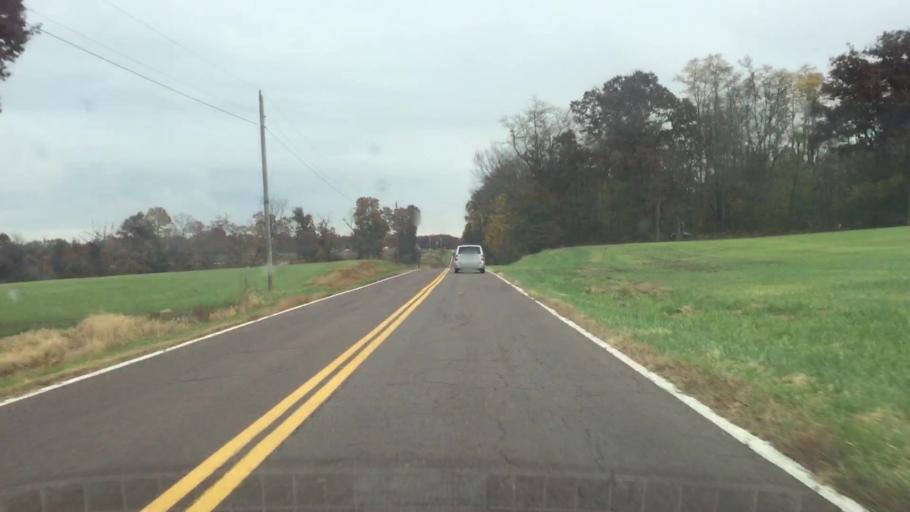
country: US
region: Missouri
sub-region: Callaway County
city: Fulton
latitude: 38.7873
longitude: -91.7705
